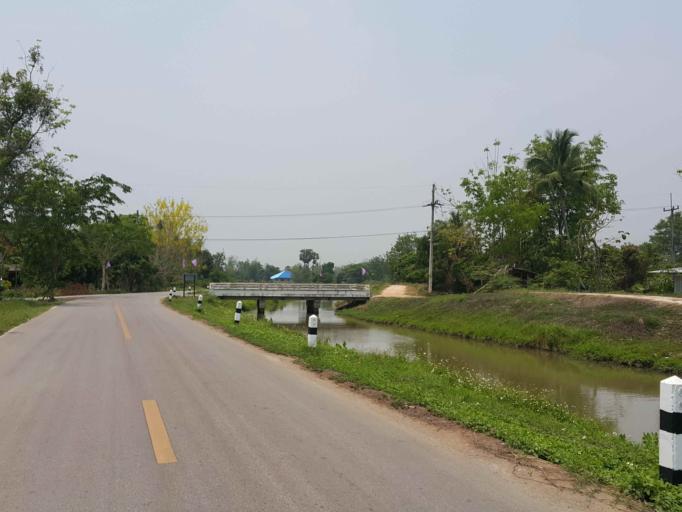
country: TH
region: Chiang Mai
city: San Sai
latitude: 18.8939
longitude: 99.0642
